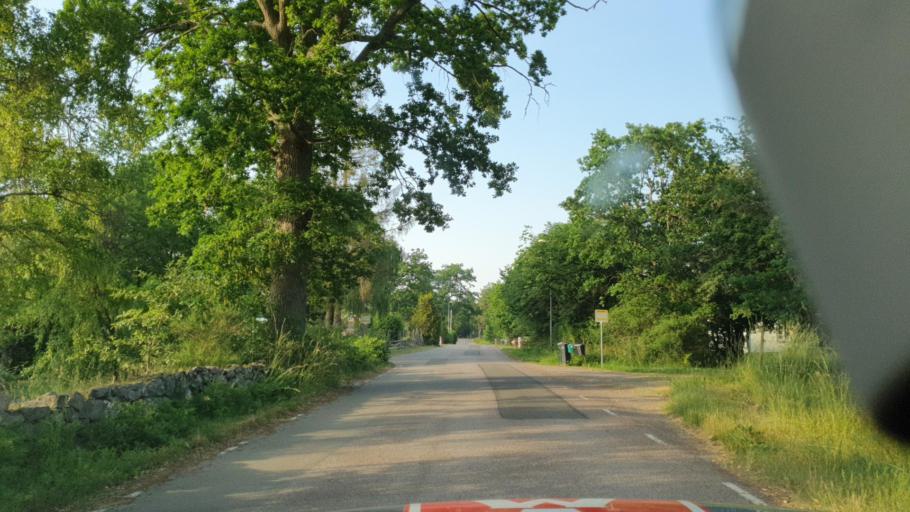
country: SE
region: Kalmar
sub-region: Kalmar Kommun
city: Ljungbyholm
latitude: 56.5030
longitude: 16.1165
